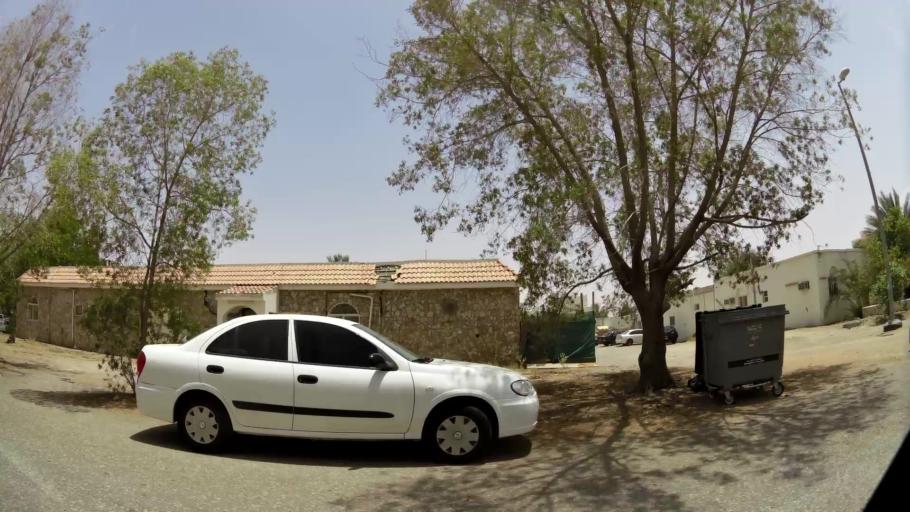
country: AE
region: Abu Dhabi
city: Al Ain
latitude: 24.2102
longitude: 55.7352
